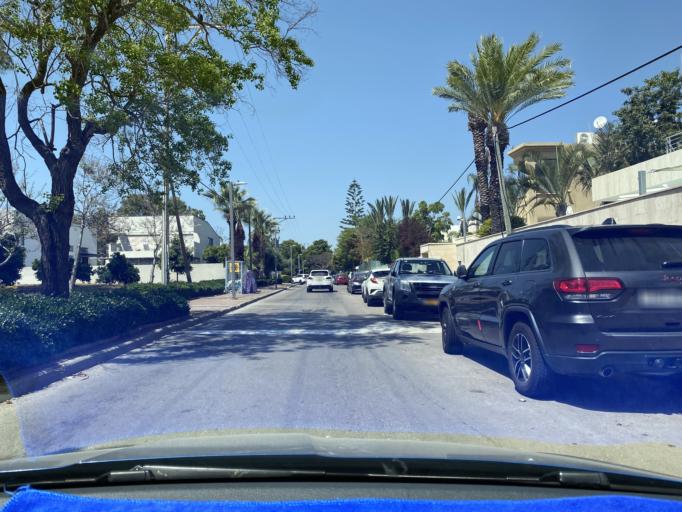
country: IL
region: Tel Aviv
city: Kefar Shemaryahu
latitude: 32.1784
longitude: 34.8147
